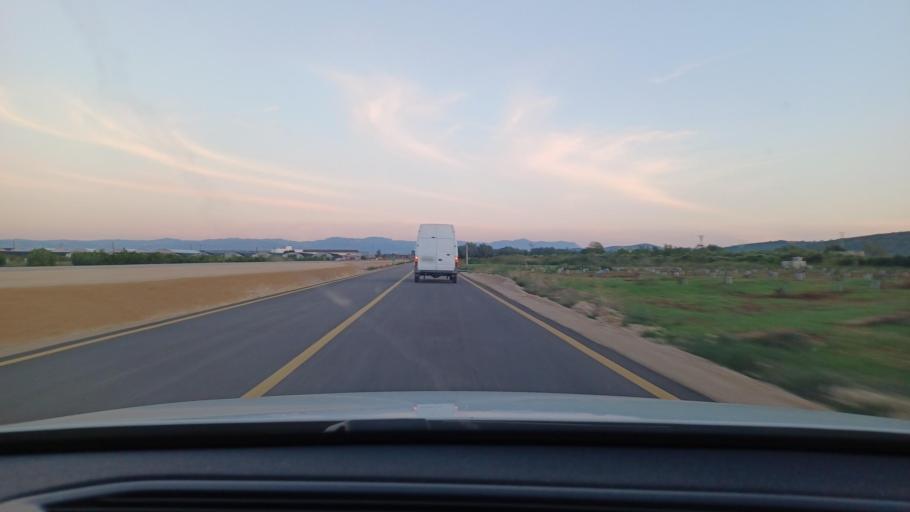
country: ES
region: Catalonia
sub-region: Provincia de Tarragona
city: Alcanar
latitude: 40.5384
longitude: 0.4405
